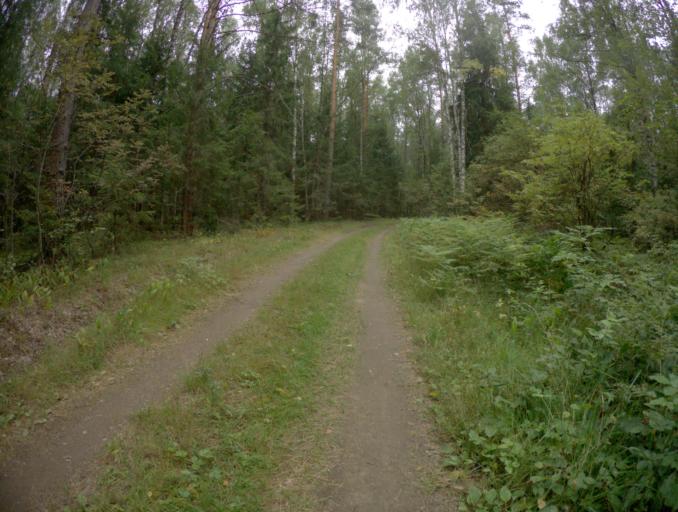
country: RU
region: Vladimir
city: Raduzhnyy
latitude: 55.9849
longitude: 40.2843
